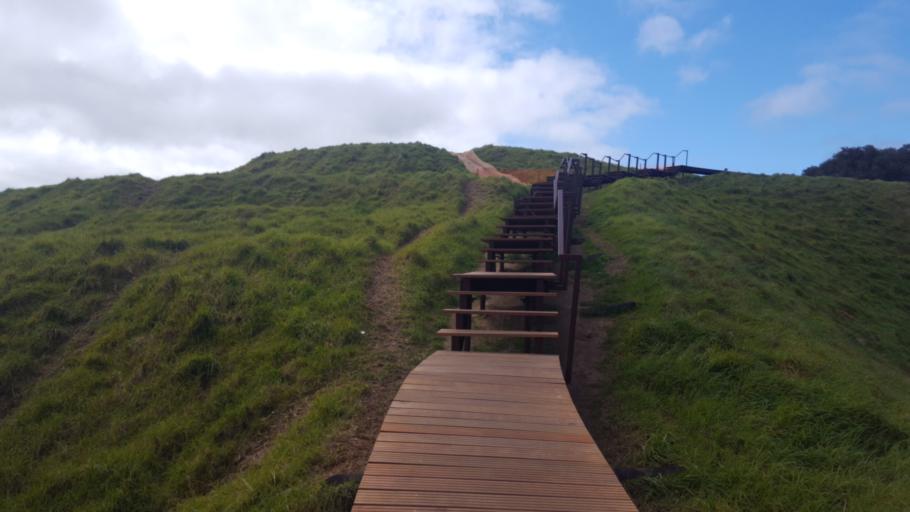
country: NZ
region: Auckland
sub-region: Auckland
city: Auckland
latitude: -36.8767
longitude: 174.7641
